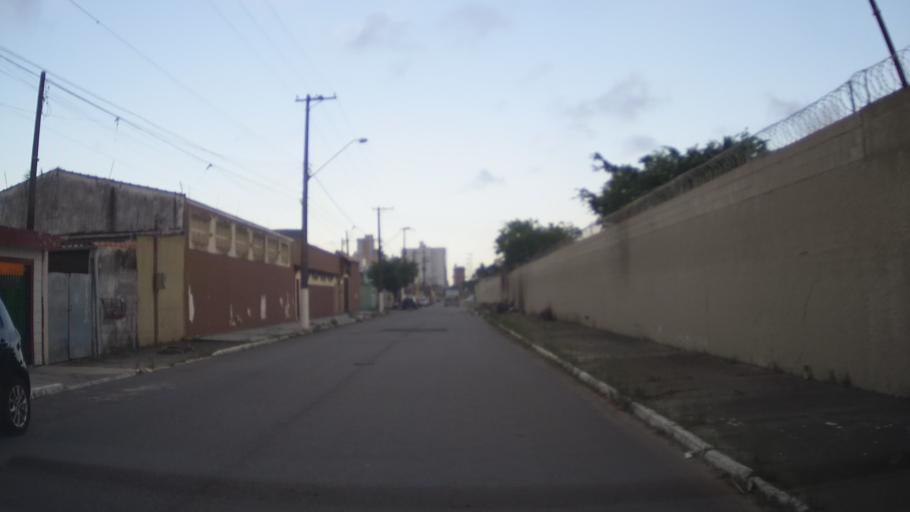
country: BR
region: Sao Paulo
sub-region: Praia Grande
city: Praia Grande
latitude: -24.0084
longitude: -46.4458
